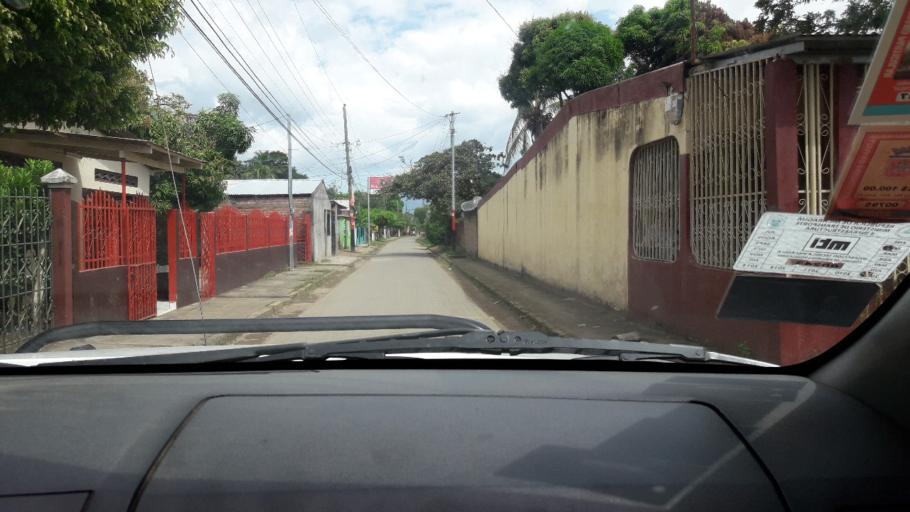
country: NI
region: Rivas
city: Rivas
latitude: 11.4494
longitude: -85.8208
